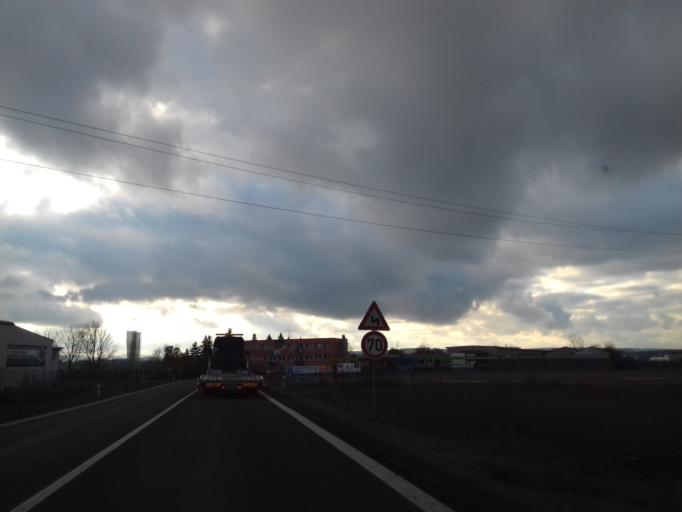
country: CZ
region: Pardubicky
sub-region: Okres Svitavy
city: Policka
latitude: 49.7202
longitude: 16.2883
